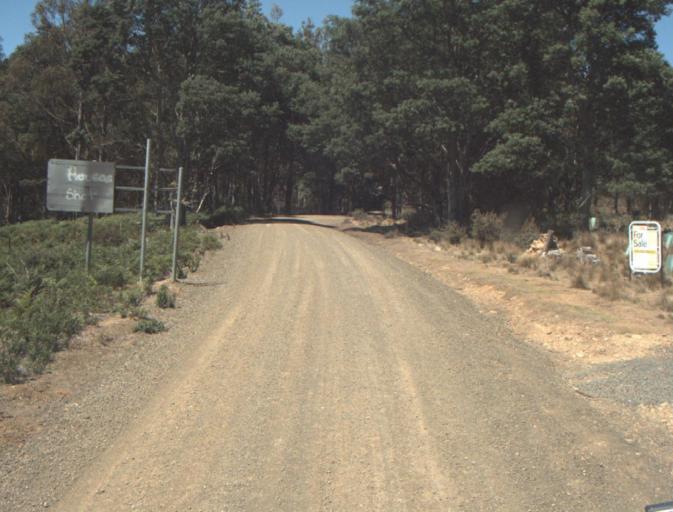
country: AU
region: Tasmania
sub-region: Dorset
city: Scottsdale
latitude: -41.3543
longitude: 147.4249
